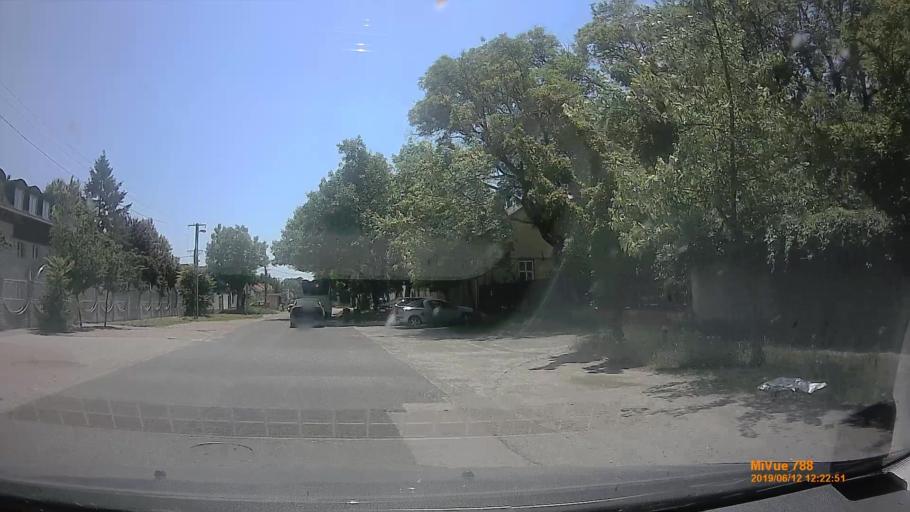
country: HU
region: Bacs-Kiskun
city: Kecskemet
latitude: 46.8958
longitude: 19.6991
